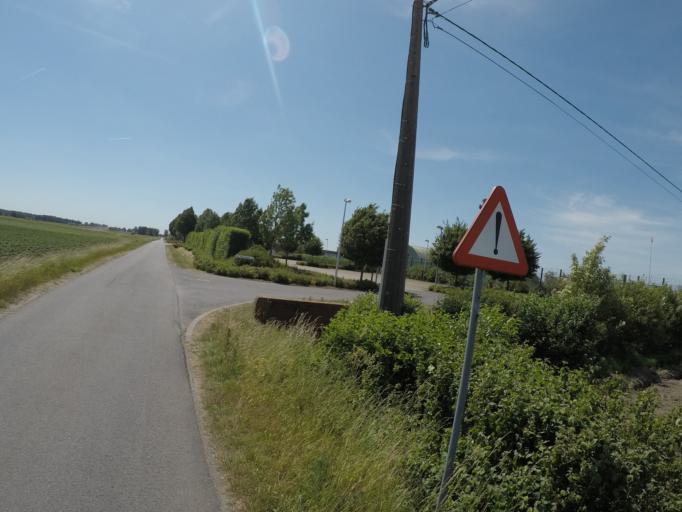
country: BE
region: Flanders
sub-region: Provincie Antwerpen
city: Hoogstraten
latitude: 51.3897
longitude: 4.7047
